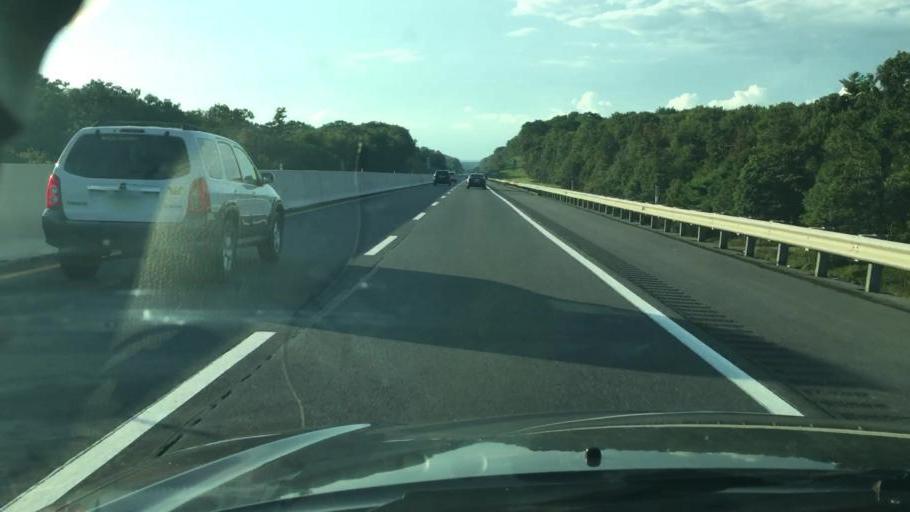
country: US
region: Pennsylvania
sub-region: Carbon County
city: Towamensing Trails
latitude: 41.0453
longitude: -75.6694
